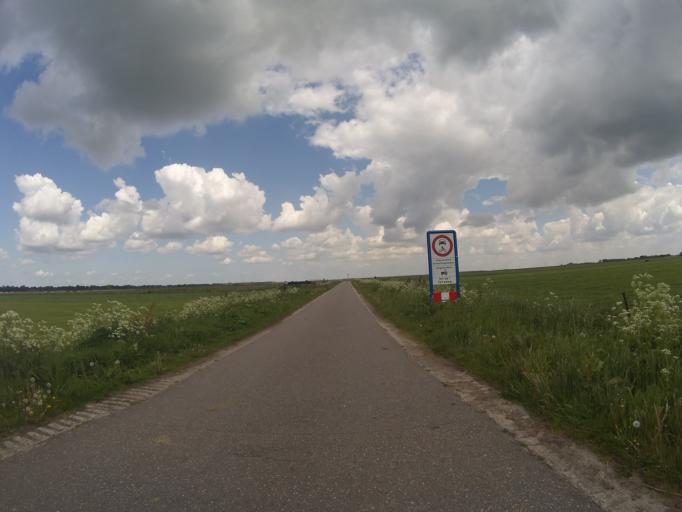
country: NL
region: Utrecht
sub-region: Gemeente Baarn
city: Baarn
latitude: 52.2449
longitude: 5.2867
